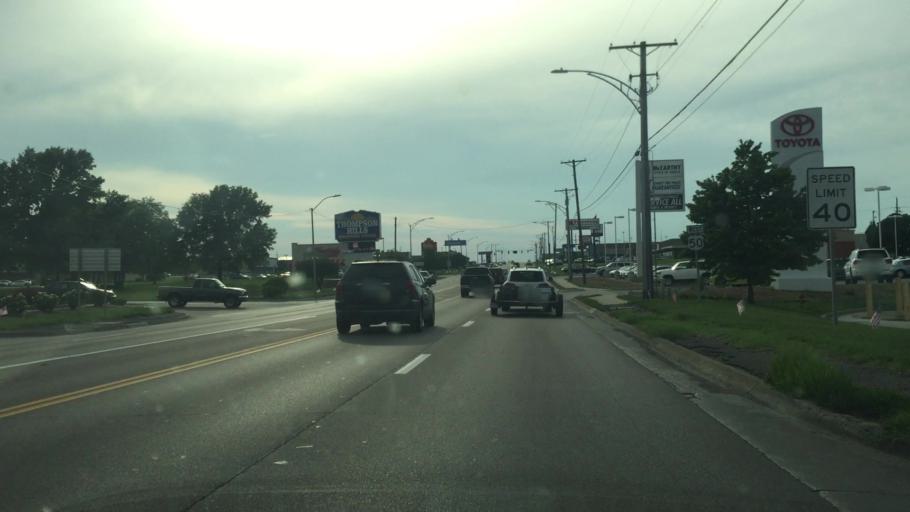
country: US
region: Missouri
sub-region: Pettis County
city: Sedalia
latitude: 38.7086
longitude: -93.2652
